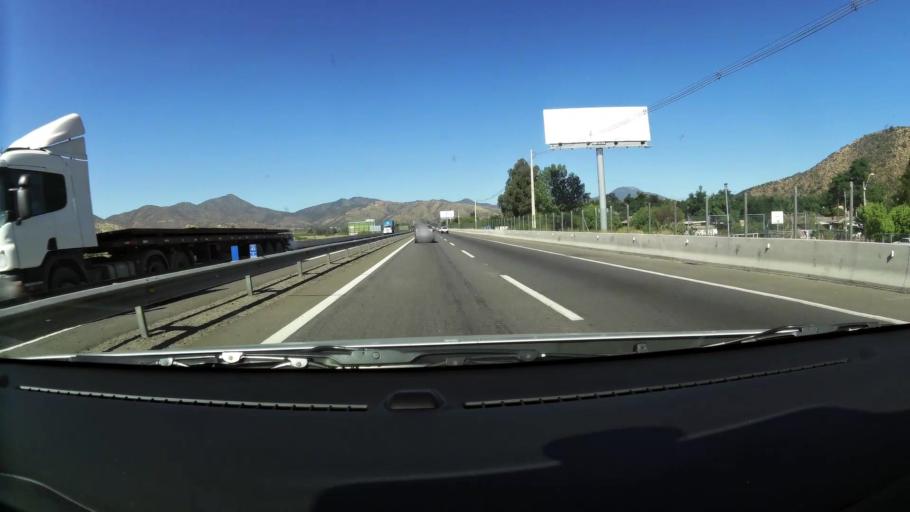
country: CL
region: Santiago Metropolitan
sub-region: Provincia de Melipilla
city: Melipilla
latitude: -33.4095
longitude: -71.1395
